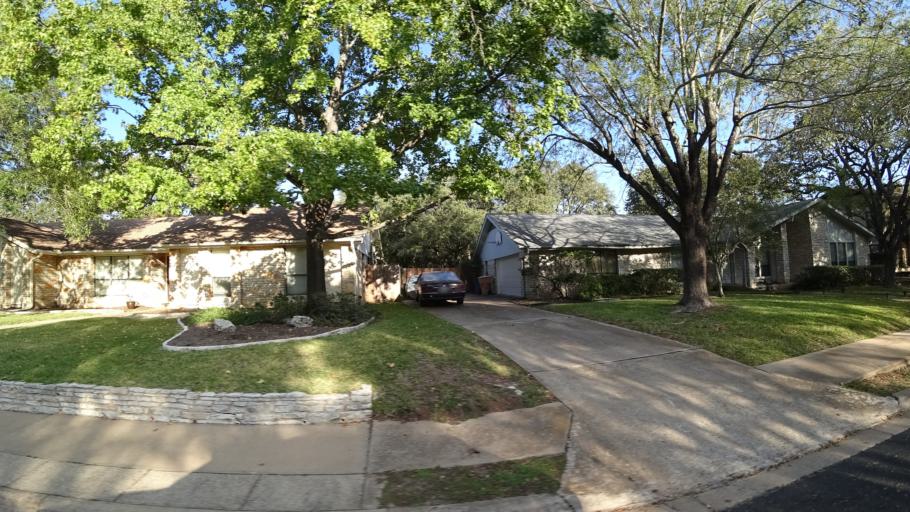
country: US
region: Texas
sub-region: Williamson County
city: Anderson Mill
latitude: 30.4359
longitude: -97.8076
